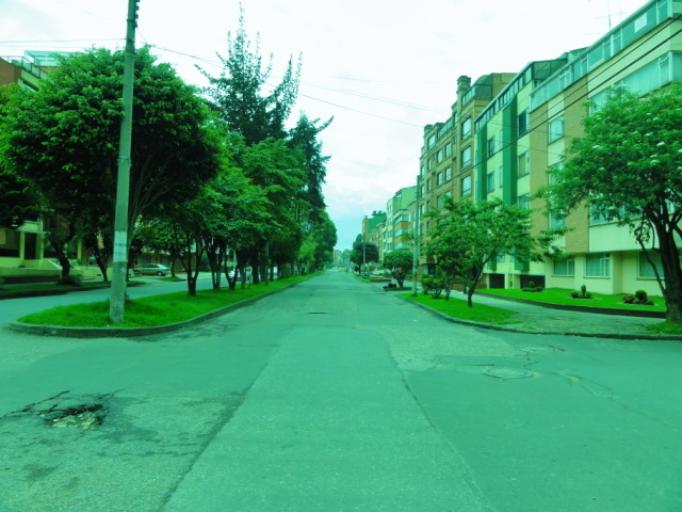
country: CO
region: Bogota D.C.
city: Bogota
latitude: 4.6461
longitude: -74.0837
